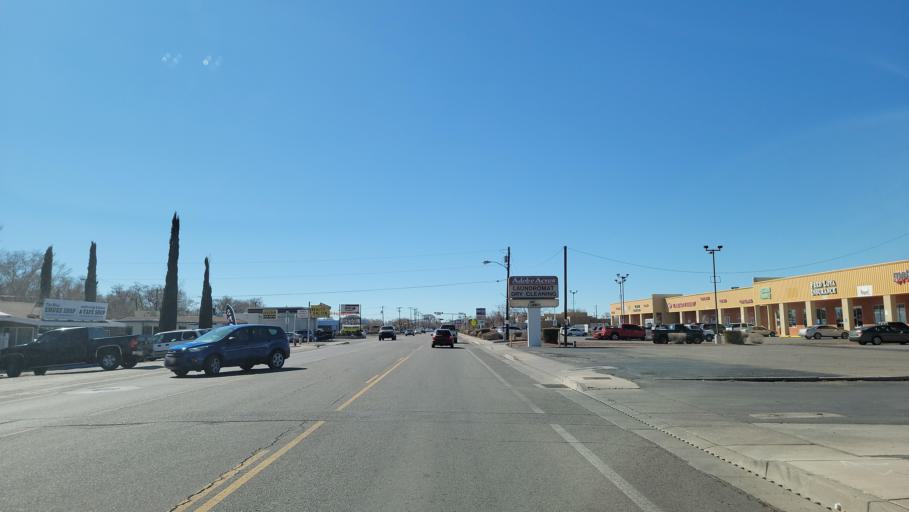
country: US
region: New Mexico
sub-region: Bernalillo County
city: South Valley
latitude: 35.0215
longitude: -106.6824
